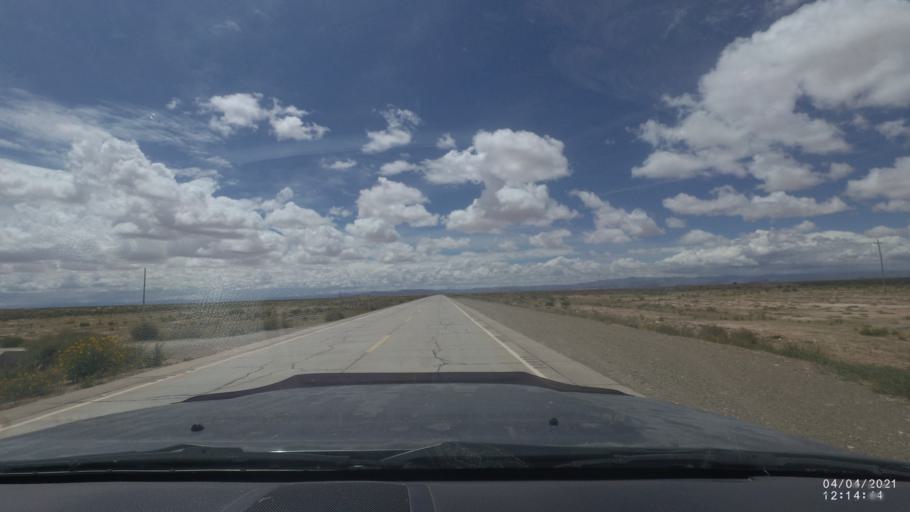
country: BO
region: Oruro
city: Oruro
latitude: -18.1304
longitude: -67.3237
